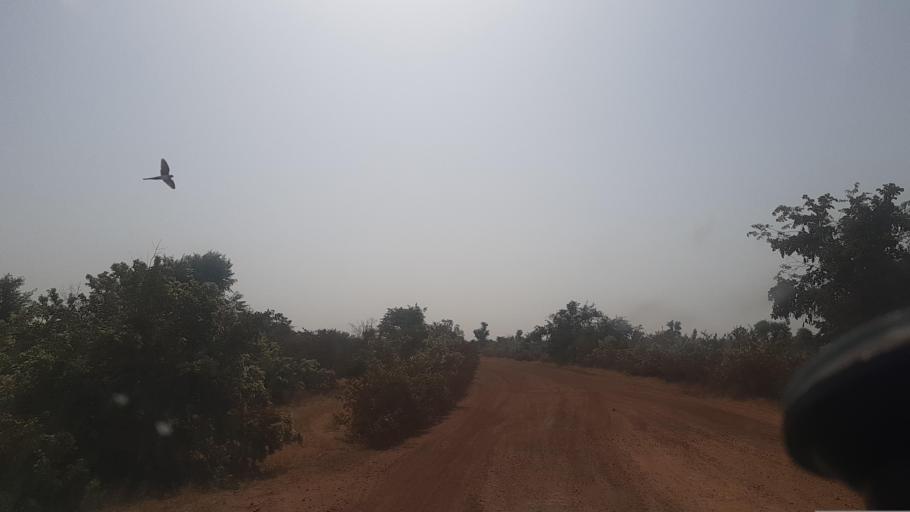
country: ML
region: Segou
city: Baroueli
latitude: 13.0602
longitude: -6.4725
